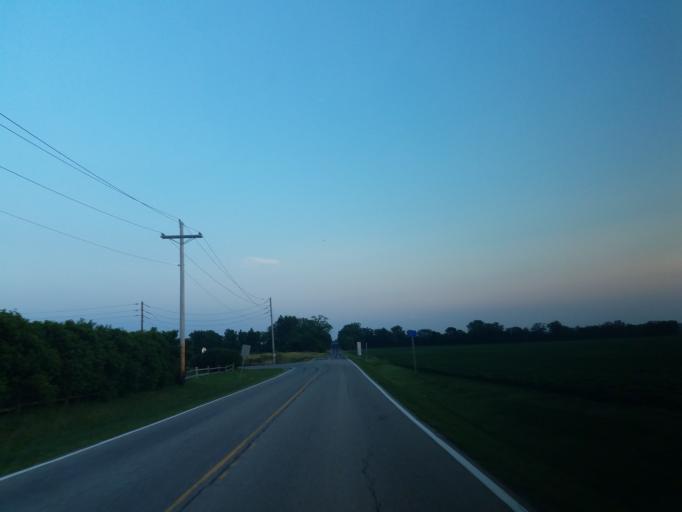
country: US
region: Illinois
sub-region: McLean County
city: Bloomington
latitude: 40.4423
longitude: -89.0055
